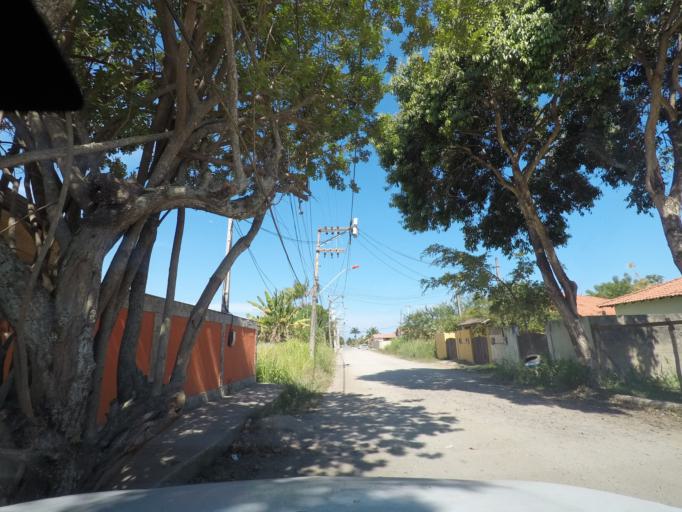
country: BR
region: Rio de Janeiro
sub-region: Marica
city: Marica
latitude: -22.9595
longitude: -42.9684
